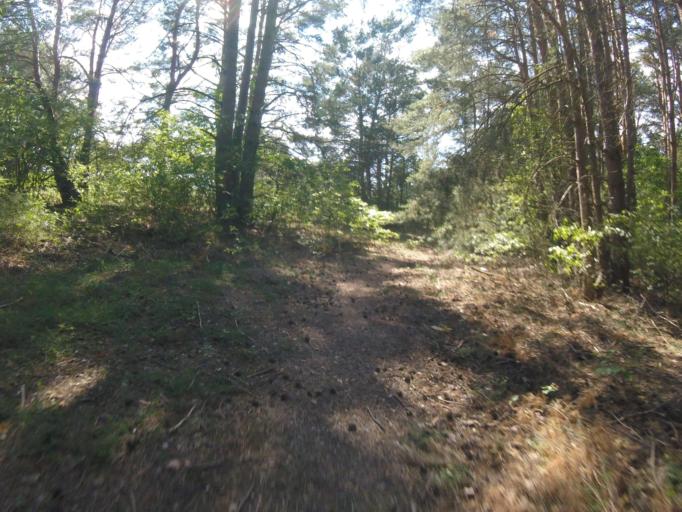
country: DE
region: Brandenburg
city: Wildau
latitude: 52.3296
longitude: 13.6593
